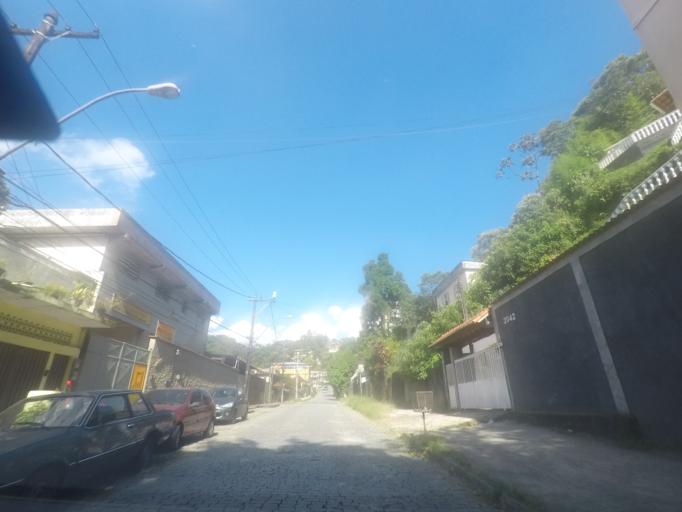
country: BR
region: Rio de Janeiro
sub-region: Petropolis
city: Petropolis
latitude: -22.5217
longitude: -43.2022
